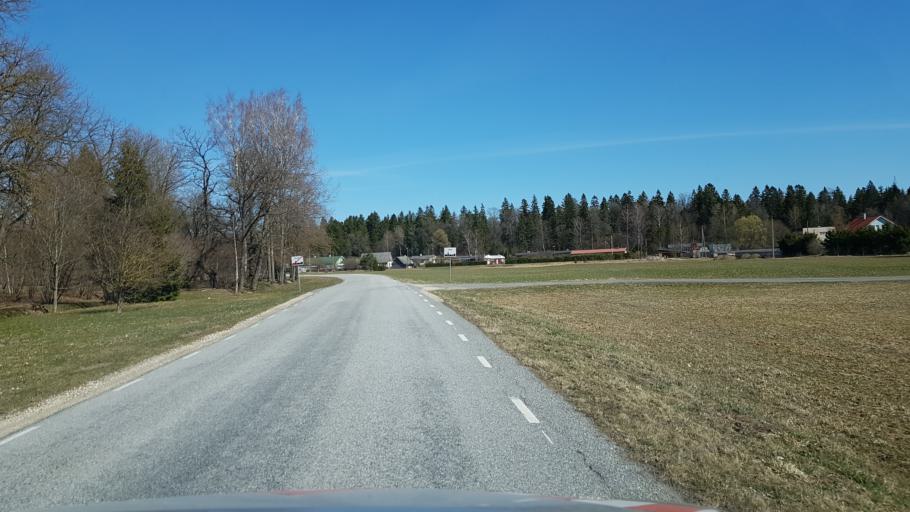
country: EE
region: Laeaene-Virumaa
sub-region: Vinni vald
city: Vinni
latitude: 59.2846
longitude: 26.4263
